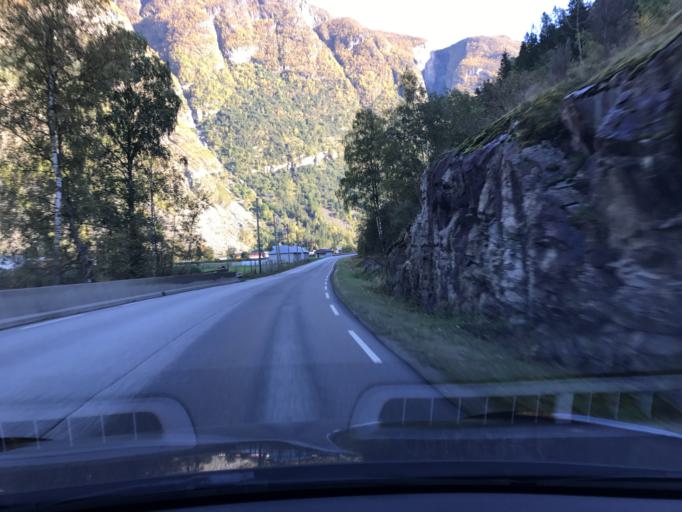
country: NO
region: Sogn og Fjordane
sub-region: Laerdal
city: Laerdalsoyri
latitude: 61.0989
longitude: 7.5134
